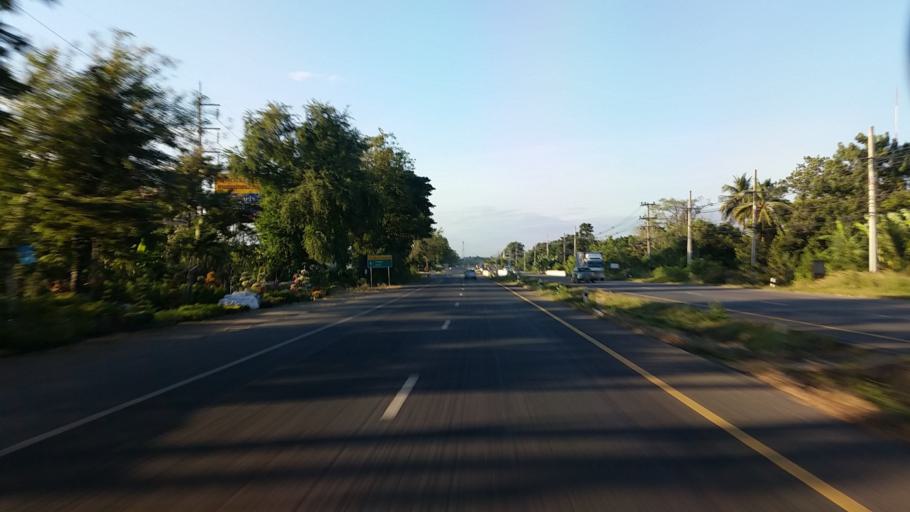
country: TH
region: Lop Buri
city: Chai Badan
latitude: 15.1799
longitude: 101.0712
